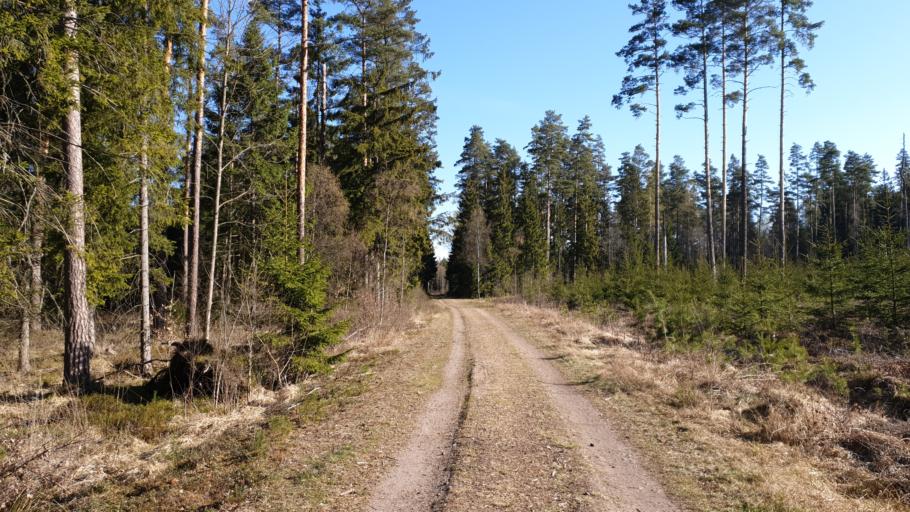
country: SE
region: Kronoberg
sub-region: Ljungby Kommun
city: Ljungby
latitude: 56.8331
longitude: 13.9036
